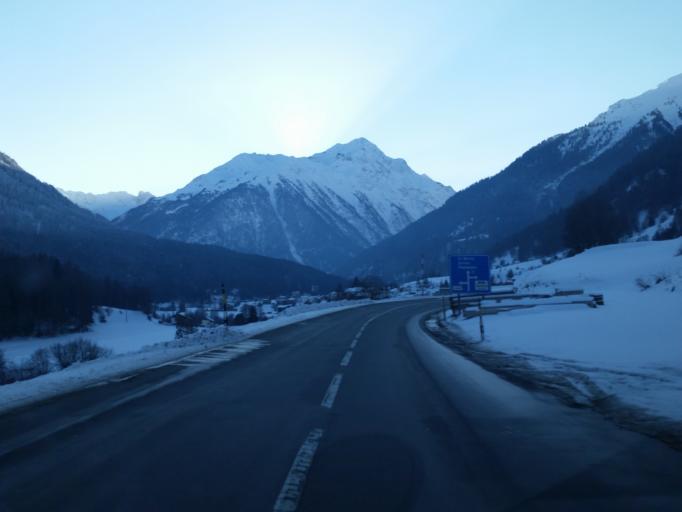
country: CH
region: Grisons
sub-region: Inn District
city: Zernez
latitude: 46.7699
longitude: 10.1192
